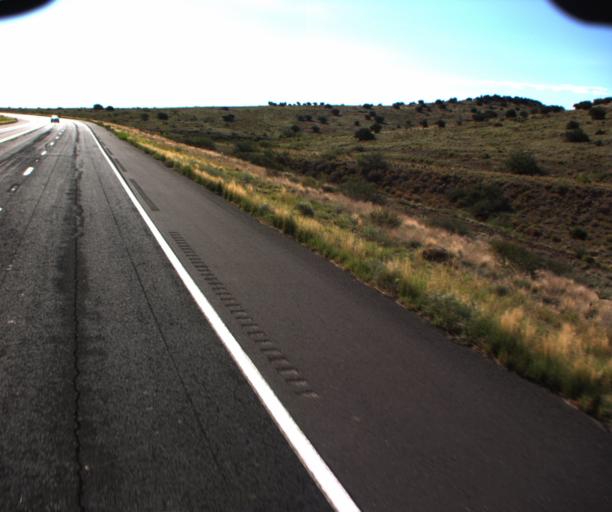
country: US
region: Arizona
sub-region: Greenlee County
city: Clifton
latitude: 32.8515
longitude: -109.3050
